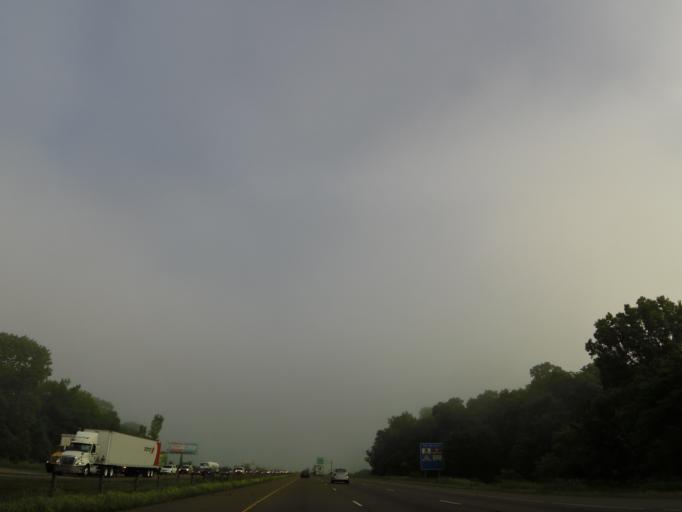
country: US
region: Minnesota
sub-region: Hennepin County
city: Rogers
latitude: 45.1781
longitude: -93.5301
